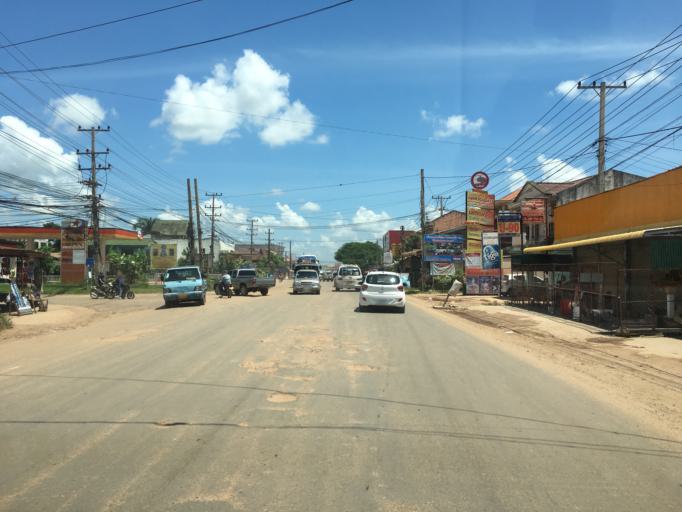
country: TH
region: Nong Khai
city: Si Chiang Mai
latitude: 18.0168
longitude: 102.5464
